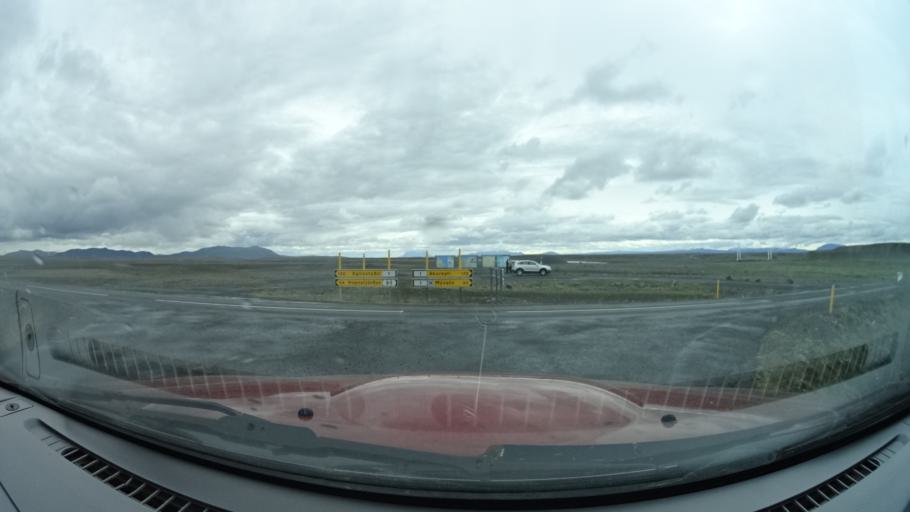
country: IS
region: Northeast
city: Laugar
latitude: 65.6263
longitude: -16.1776
